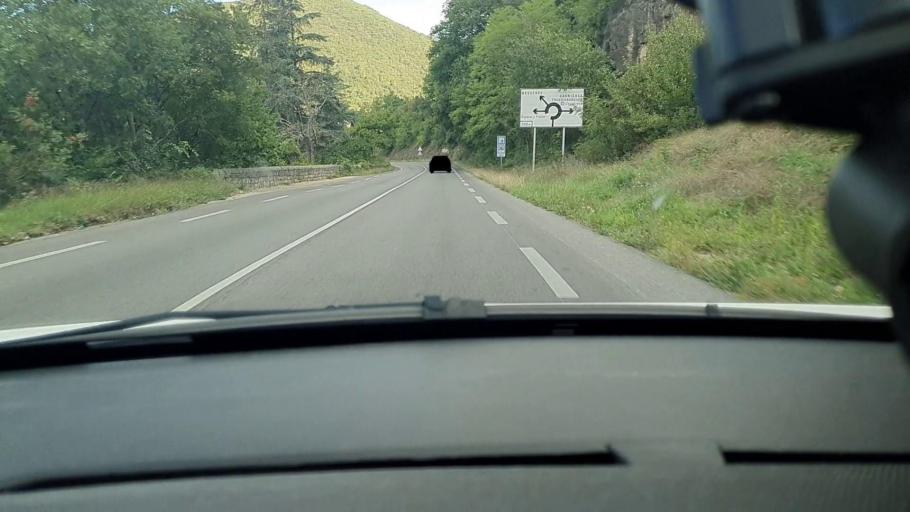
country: FR
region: Languedoc-Roussillon
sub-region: Departement du Gard
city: Besseges
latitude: 44.2828
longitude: 4.1278
